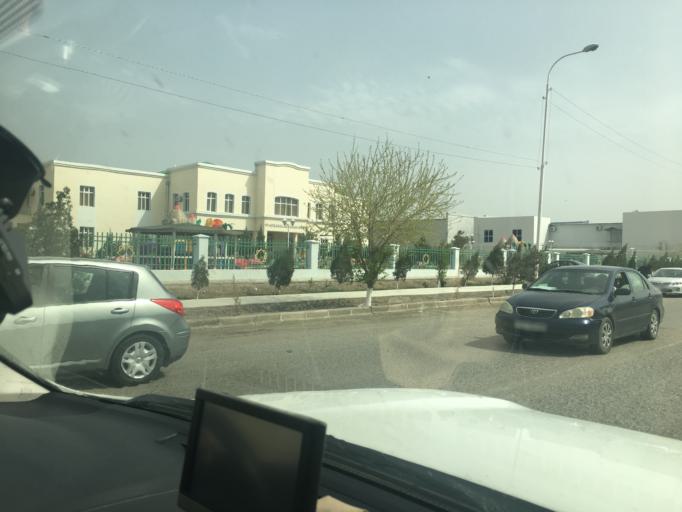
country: TM
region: Mary
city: Mary
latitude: 37.5961
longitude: 61.8562
